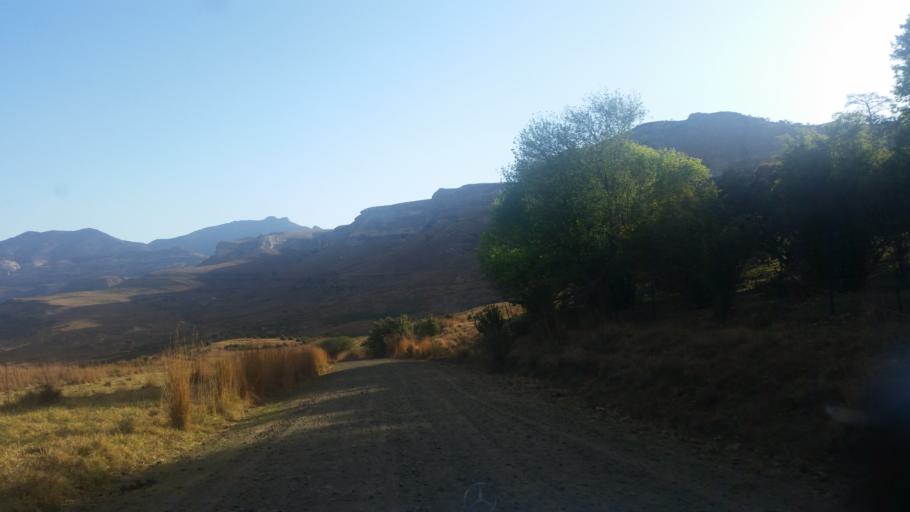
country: ZA
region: Orange Free State
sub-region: Thabo Mofutsanyana District Municipality
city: Phuthaditjhaba
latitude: -28.4934
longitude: 28.6900
